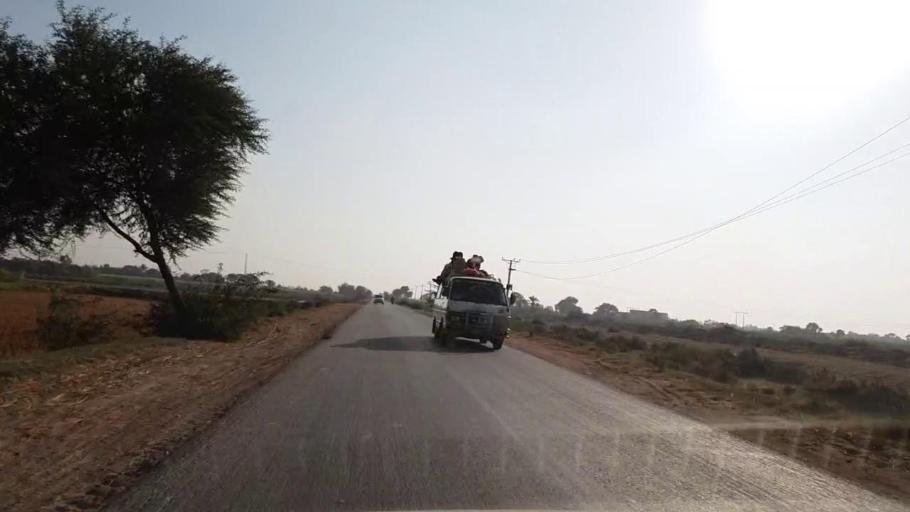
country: PK
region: Sindh
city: Bulri
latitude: 24.8939
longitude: 68.3446
